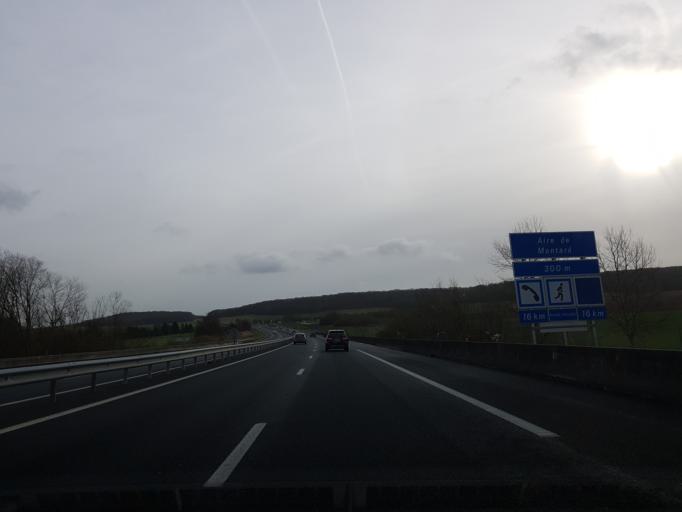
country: FR
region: Bourgogne
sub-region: Departement de l'Yonne
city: Soucy
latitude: 48.2498
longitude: 3.3422
